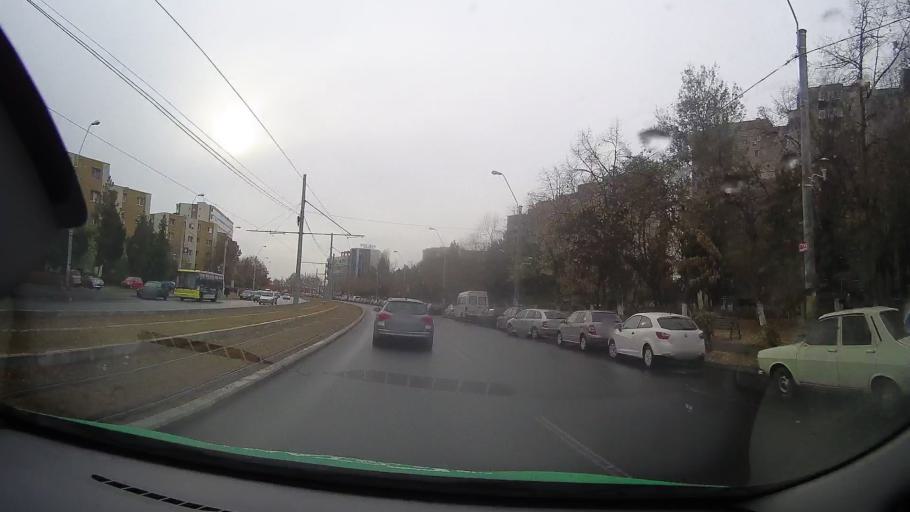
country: RO
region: Prahova
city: Ploiesti
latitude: 44.9307
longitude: 25.9893
